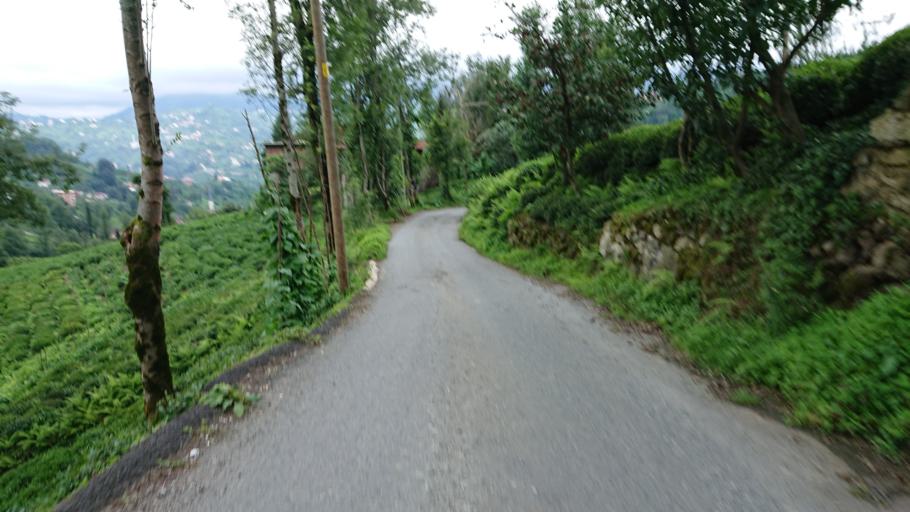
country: TR
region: Rize
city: Rize
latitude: 40.9662
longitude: 40.5122
